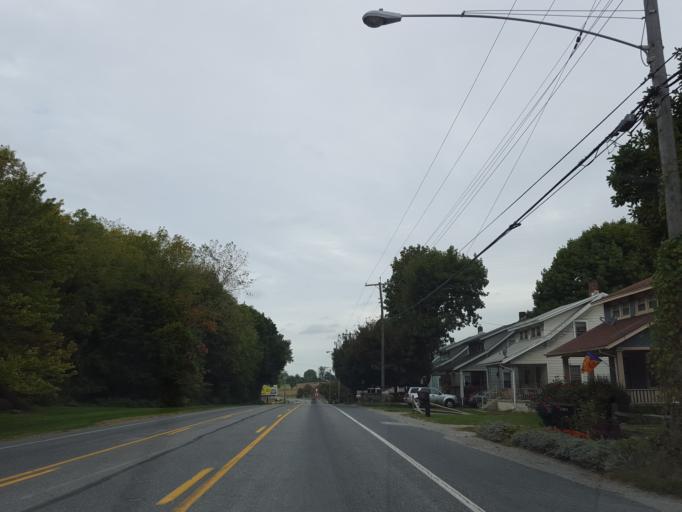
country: US
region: Pennsylvania
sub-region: York County
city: Spring Grove
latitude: 39.9277
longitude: -76.8592
